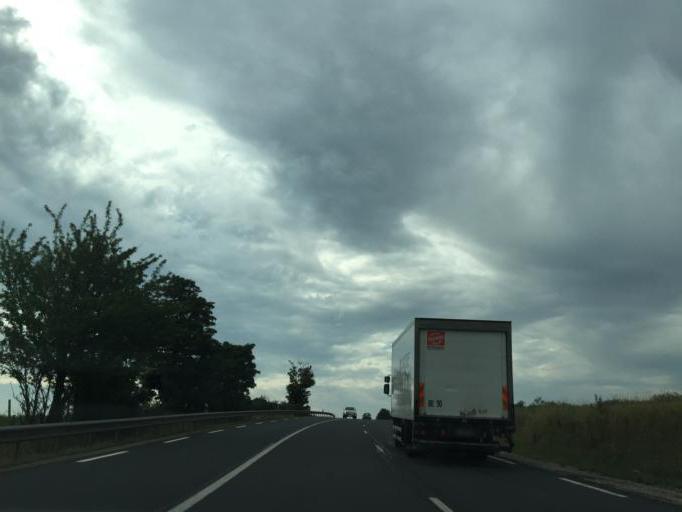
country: FR
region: Auvergne
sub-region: Departement de la Haute-Loire
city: Solignac-sur-Loire
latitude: 44.9140
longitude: 3.8474
